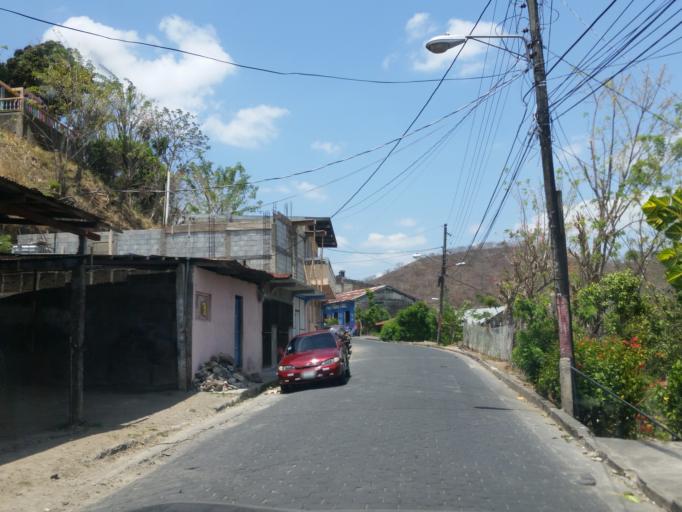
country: NI
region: Boaco
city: Boaco
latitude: 12.4742
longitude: -85.6575
